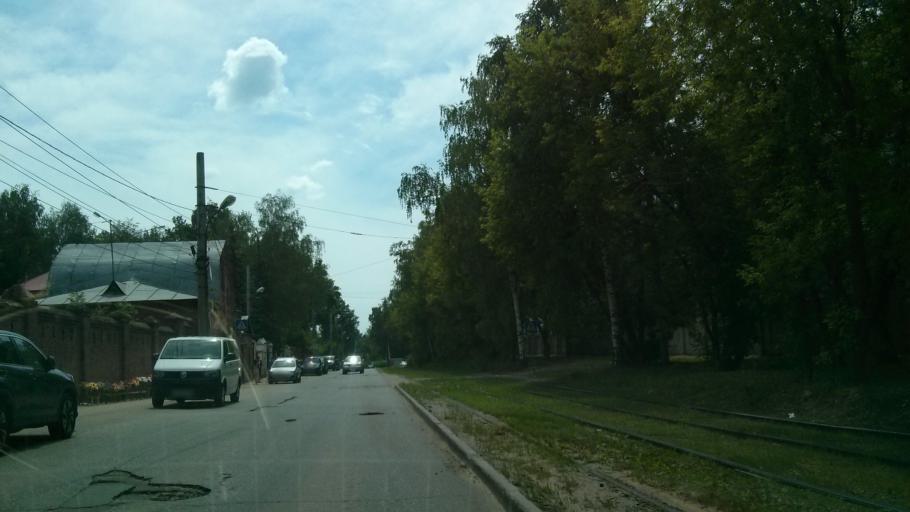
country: RU
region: Nizjnij Novgorod
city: Nizhniy Novgorod
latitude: 56.3003
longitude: 43.9915
